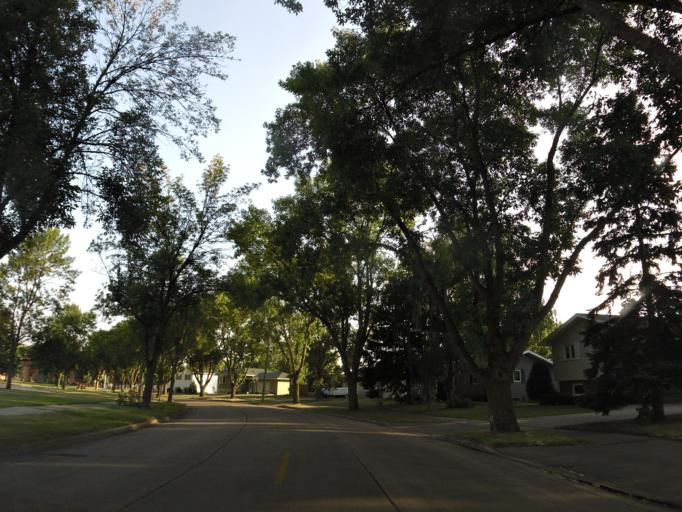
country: US
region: North Dakota
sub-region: Grand Forks County
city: Grand Forks
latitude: 47.8910
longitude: -97.0408
